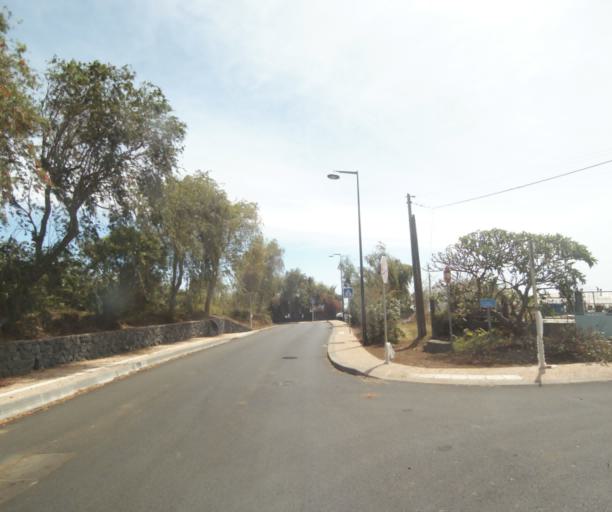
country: RE
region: Reunion
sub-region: Reunion
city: Saint-Paul
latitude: -21.0403
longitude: 55.3024
